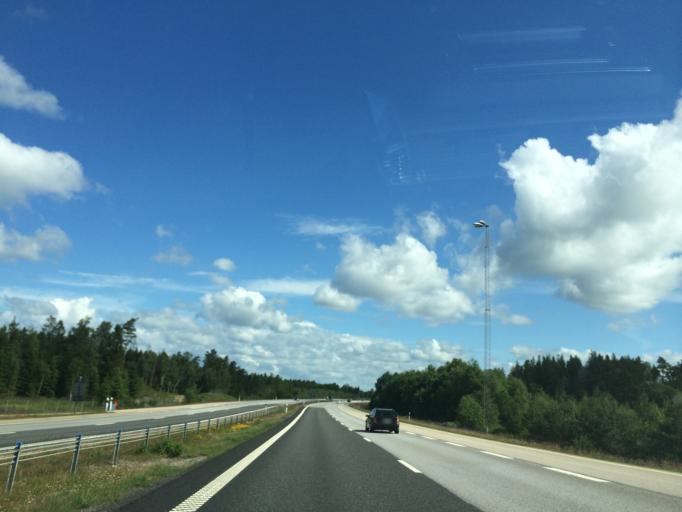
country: SE
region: Kronoberg
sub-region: Markaryds Kommun
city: Stromsnasbruk
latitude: 56.6249
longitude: 13.7854
